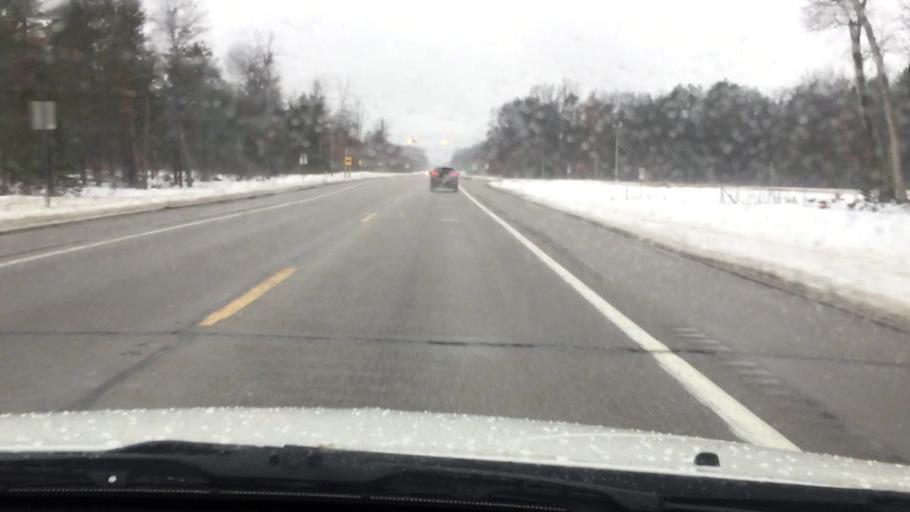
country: US
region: Michigan
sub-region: Wexford County
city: Manton
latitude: 44.5250
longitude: -85.3900
